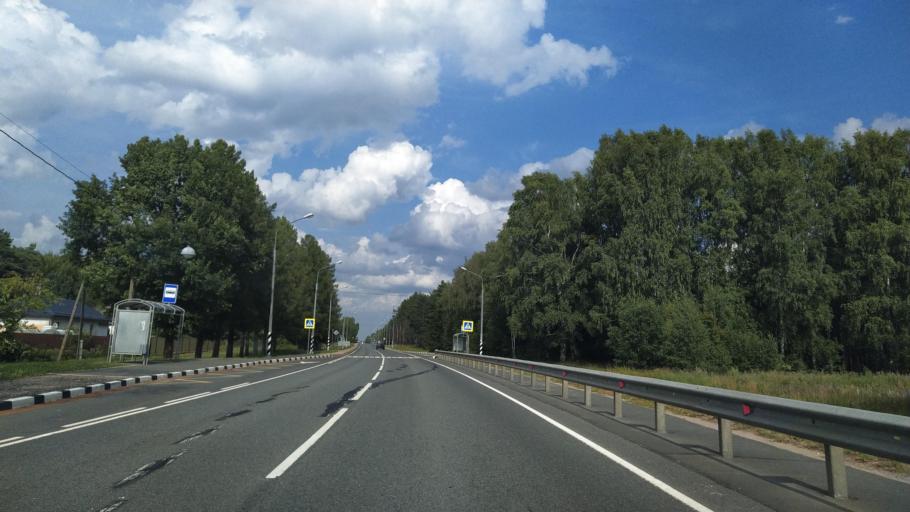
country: RU
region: Novgorod
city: Shimsk
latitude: 58.1775
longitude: 30.5301
